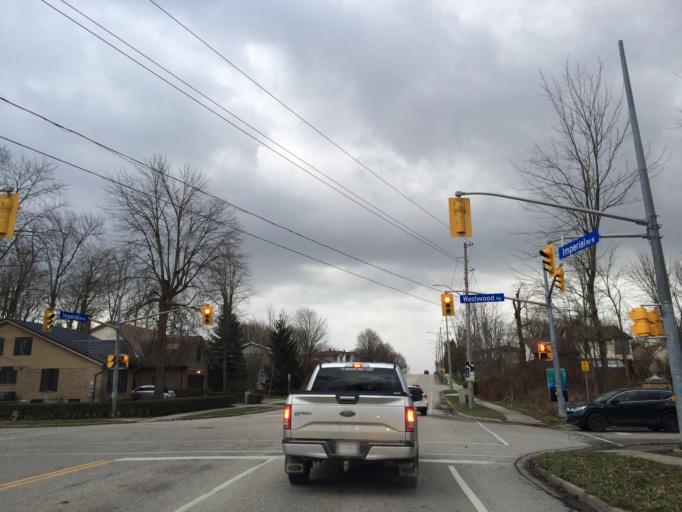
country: CA
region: Ontario
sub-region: Wellington County
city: Guelph
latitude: 43.5350
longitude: -80.2948
